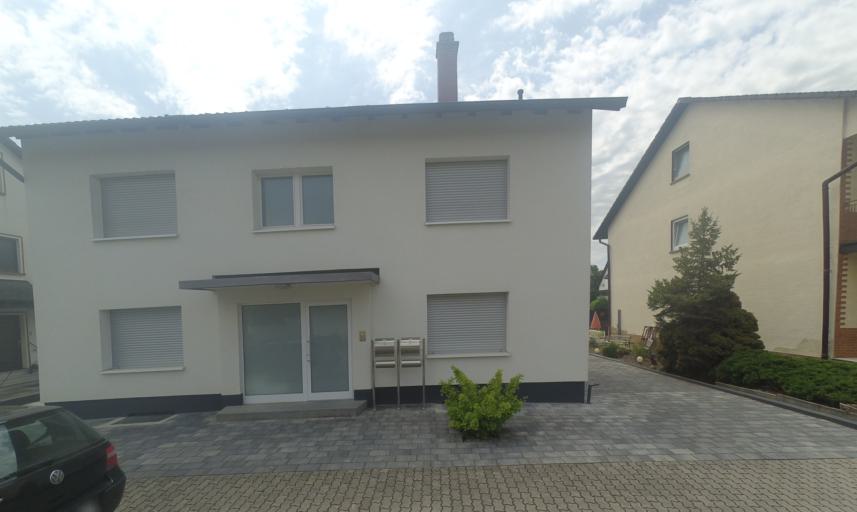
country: DE
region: Baden-Wuerttemberg
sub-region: Karlsruhe Region
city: Ketsch
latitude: 49.3729
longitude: 8.5364
